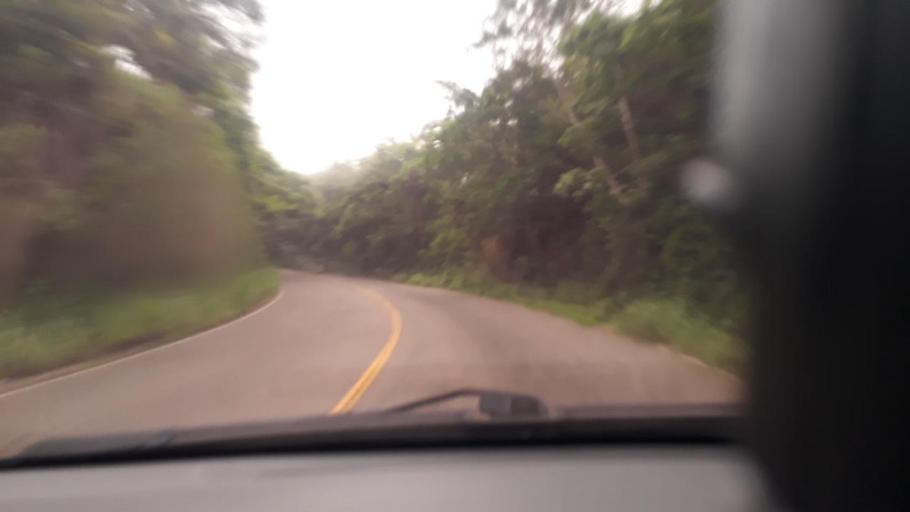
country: GT
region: Jutiapa
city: Jalpatagua
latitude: 14.1766
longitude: -90.0456
